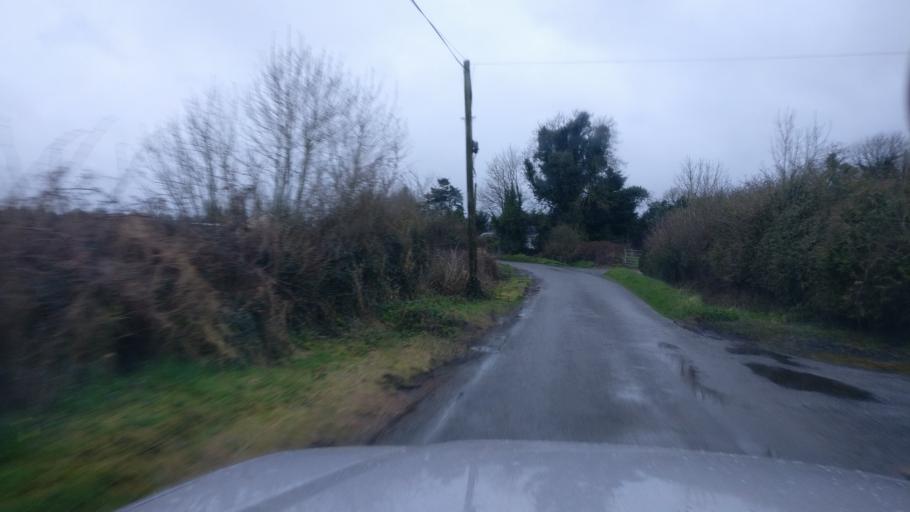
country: IE
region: Connaught
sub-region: County Galway
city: Ballinasloe
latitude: 53.2627
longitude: -8.3724
